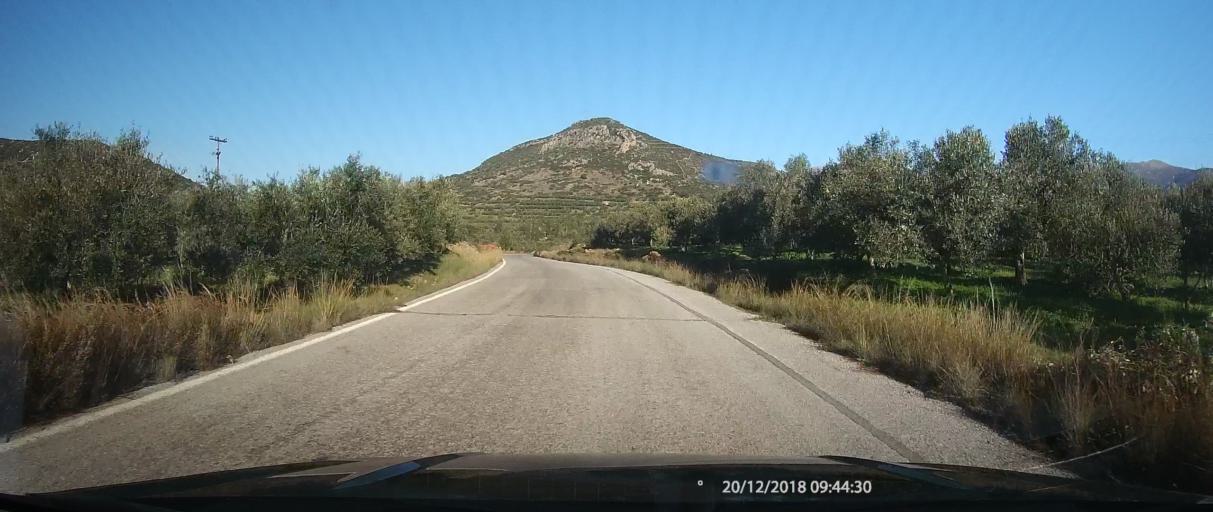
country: GR
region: Peloponnese
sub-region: Nomos Lakonias
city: Yerakion
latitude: 36.9764
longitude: 22.7372
